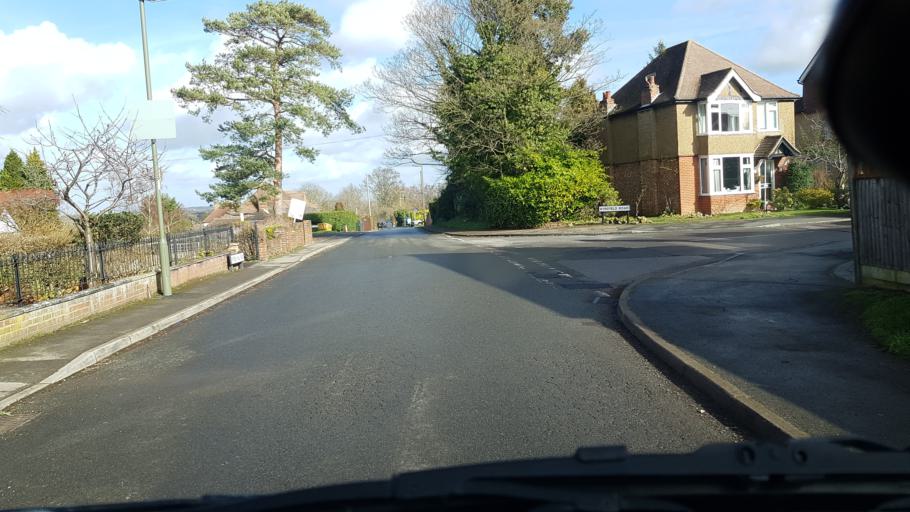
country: GB
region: England
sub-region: Surrey
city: Guildford
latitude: 51.2564
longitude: -0.6002
